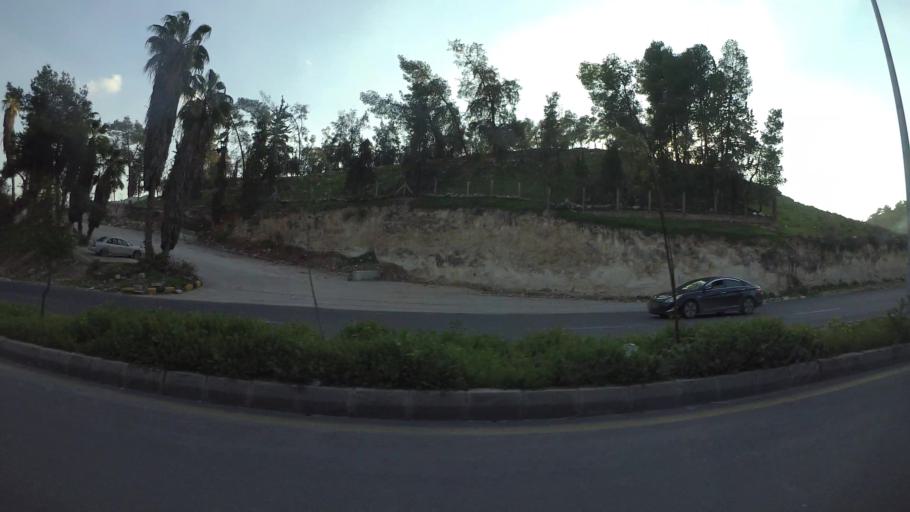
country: JO
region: Amman
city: Amman
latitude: 31.9815
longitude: 35.9707
